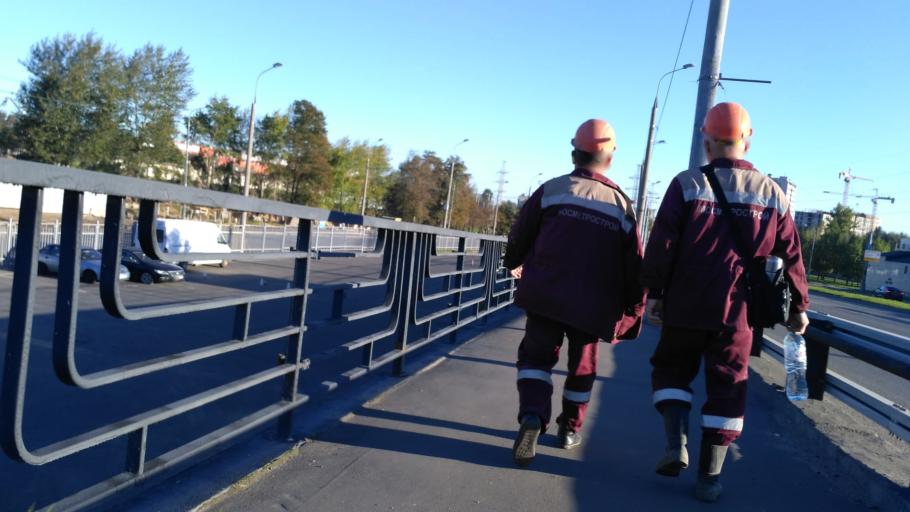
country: RU
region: Moscow
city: Novovladykino
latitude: 55.8351
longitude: 37.5782
